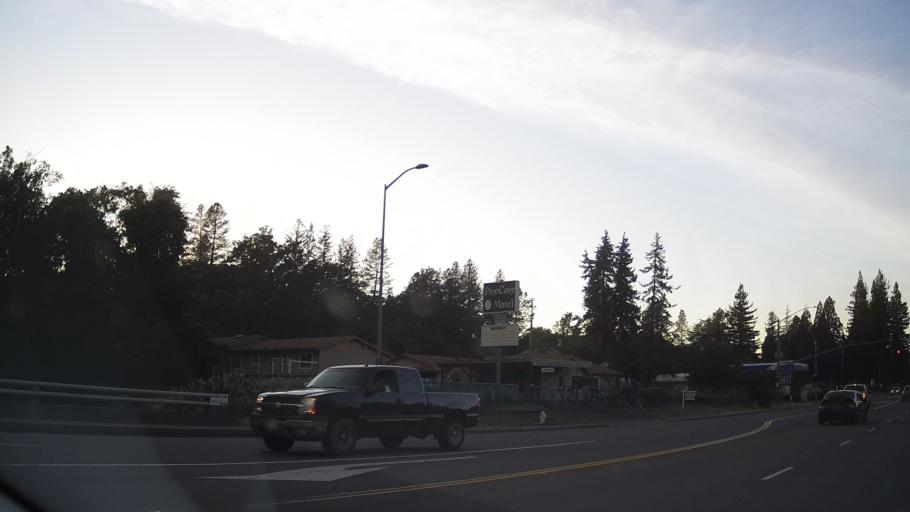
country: US
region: California
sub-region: Mendocino County
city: Willits
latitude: 39.3976
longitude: -123.3494
